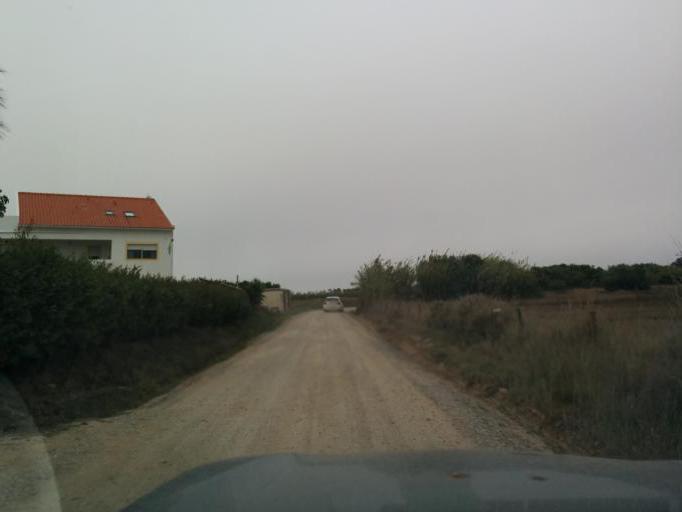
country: PT
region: Beja
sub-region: Odemira
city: Sao Teotonio
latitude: 37.5023
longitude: -8.7874
